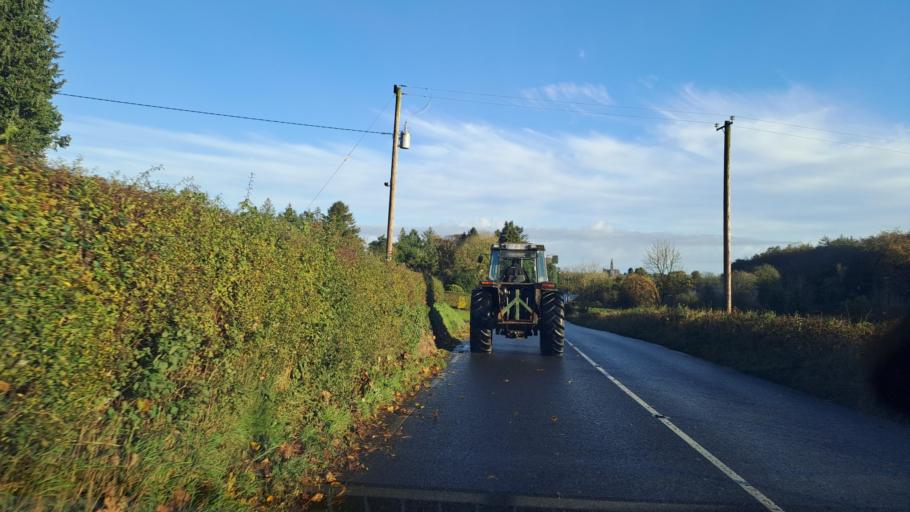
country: IE
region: Ulster
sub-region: County Monaghan
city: Monaghan
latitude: 54.2252
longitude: -6.9726
